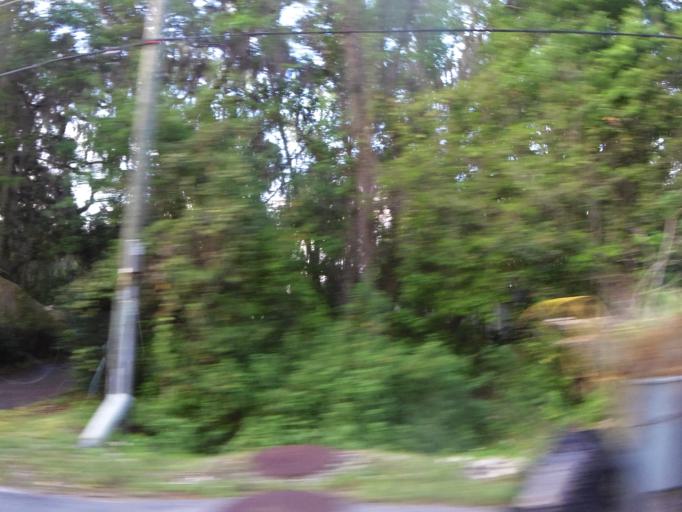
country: US
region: Florida
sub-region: Saint Johns County
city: Fruit Cove
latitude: 30.1283
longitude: -81.6148
